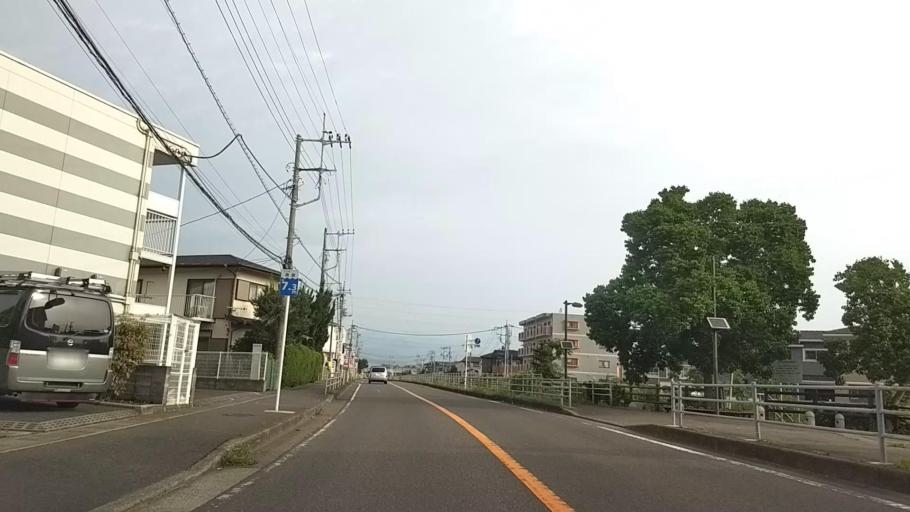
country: JP
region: Kanagawa
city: Hiratsuka
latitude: 35.3384
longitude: 139.3098
